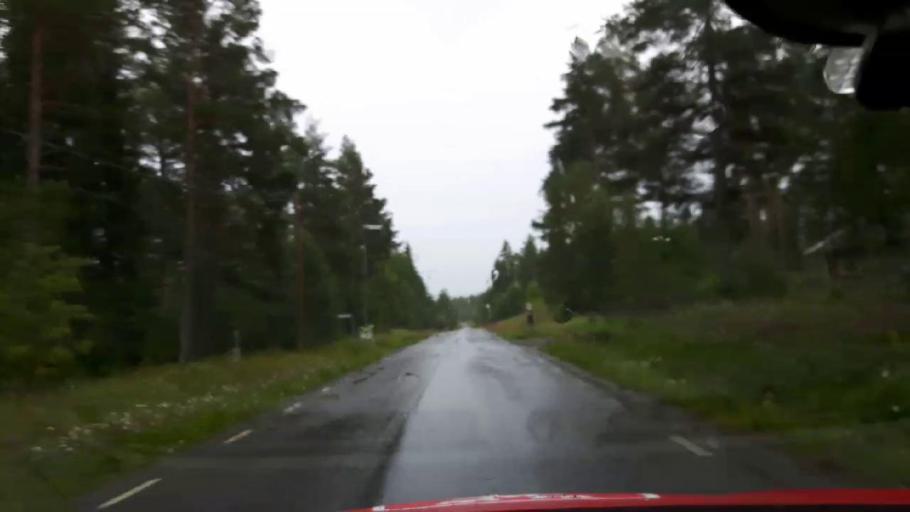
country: SE
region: Jaemtland
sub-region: OEstersunds Kommun
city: Brunflo
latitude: 62.9823
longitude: 14.8210
